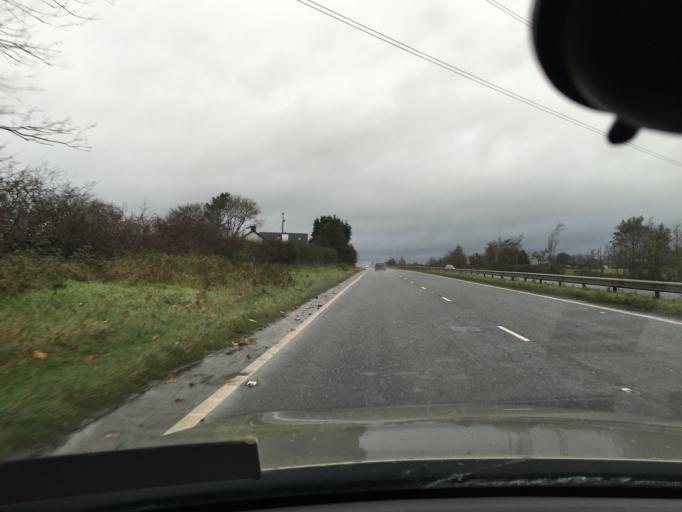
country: GB
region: Northern Ireland
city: Carnmoney
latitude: 54.7189
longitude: -5.9686
